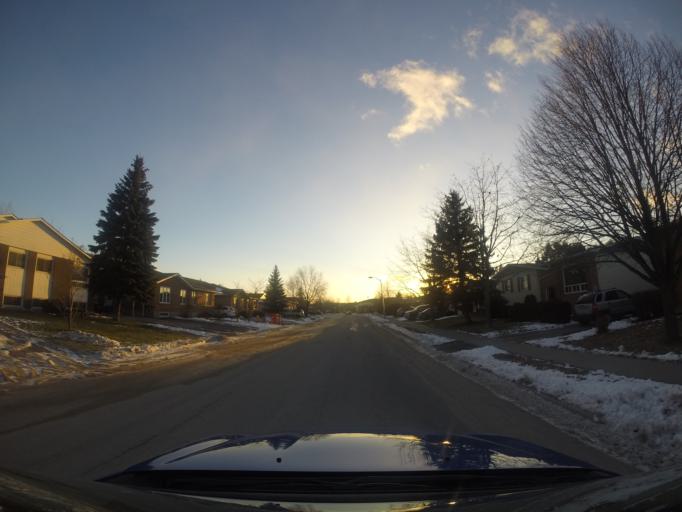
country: CA
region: Ontario
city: Greater Sudbury
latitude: 46.4995
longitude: -80.9288
